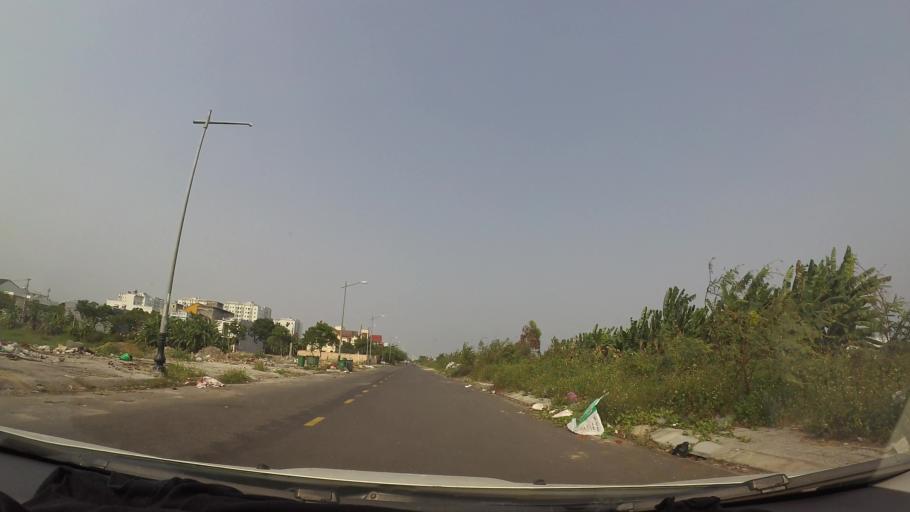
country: VN
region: Da Nang
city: Cam Le
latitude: 16.0029
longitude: 108.1959
